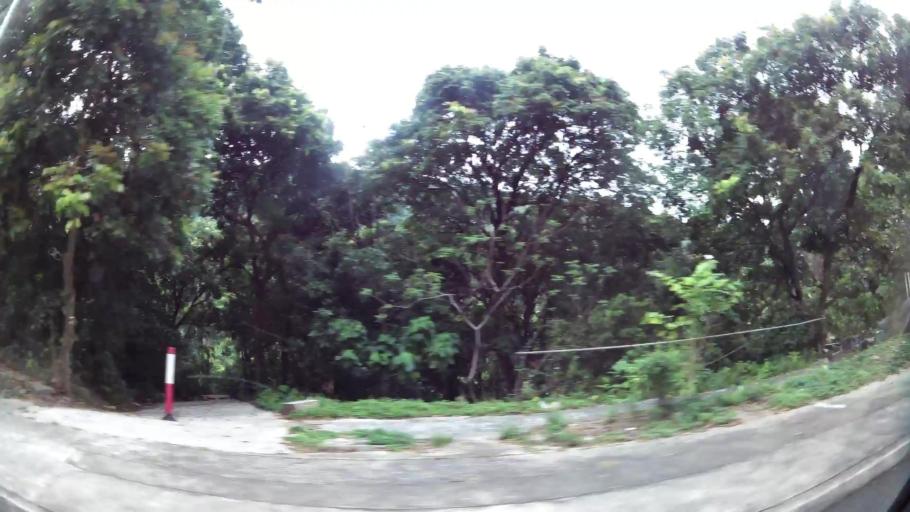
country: HK
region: Sha Tin
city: Sha Tin
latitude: 22.4018
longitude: 114.1979
